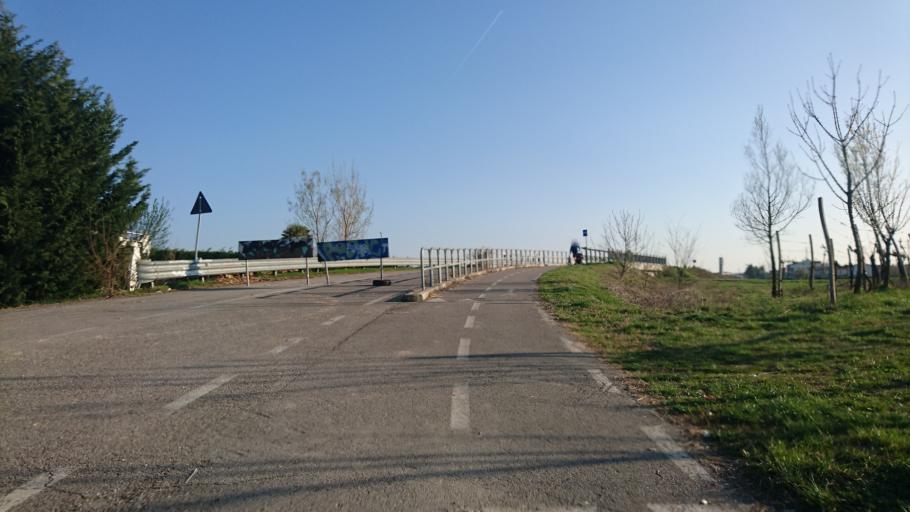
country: IT
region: Veneto
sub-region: Provincia di Padova
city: Vigonza
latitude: 45.4346
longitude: 11.9781
